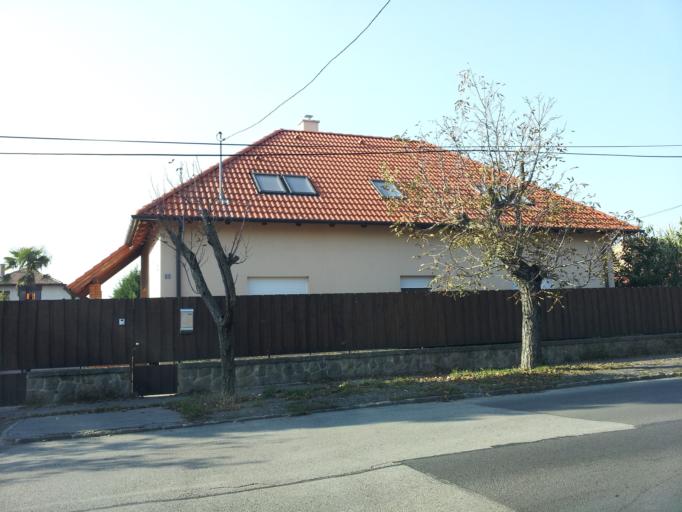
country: HU
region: Budapest
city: Budapest XVIII. keruelet
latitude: 47.4625
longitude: 19.1780
